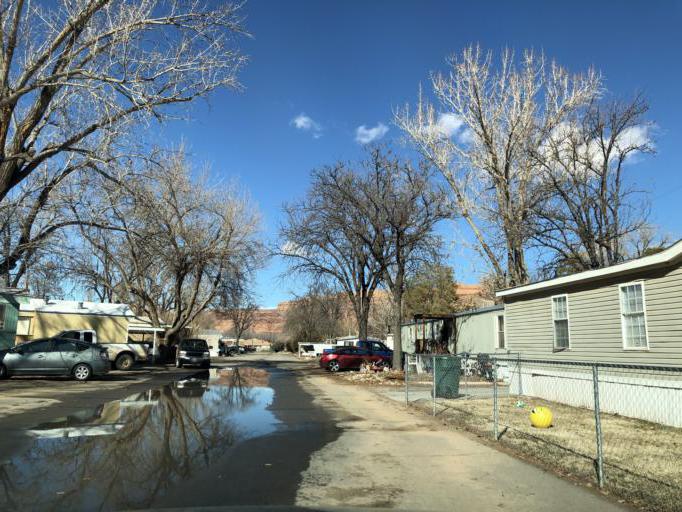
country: US
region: Utah
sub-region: Grand County
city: Moab
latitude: 38.5774
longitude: -109.5655
